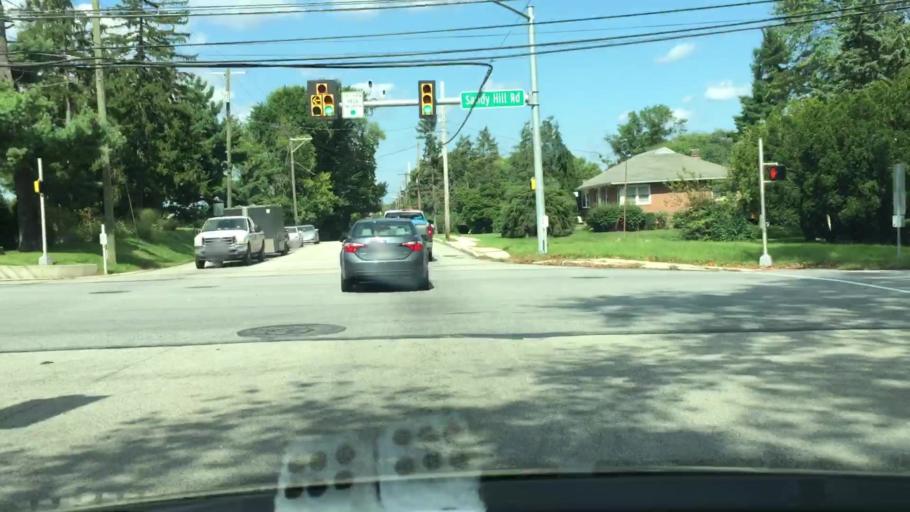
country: US
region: Pennsylvania
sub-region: Montgomery County
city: Norristown
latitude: 40.1179
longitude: -75.3071
